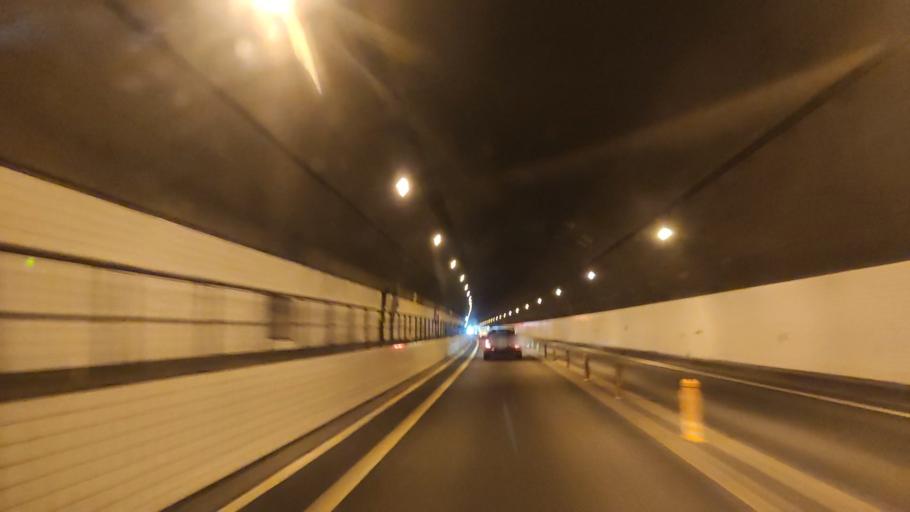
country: JP
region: Tokushima
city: Ikedacho
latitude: 34.0215
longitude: 133.7675
